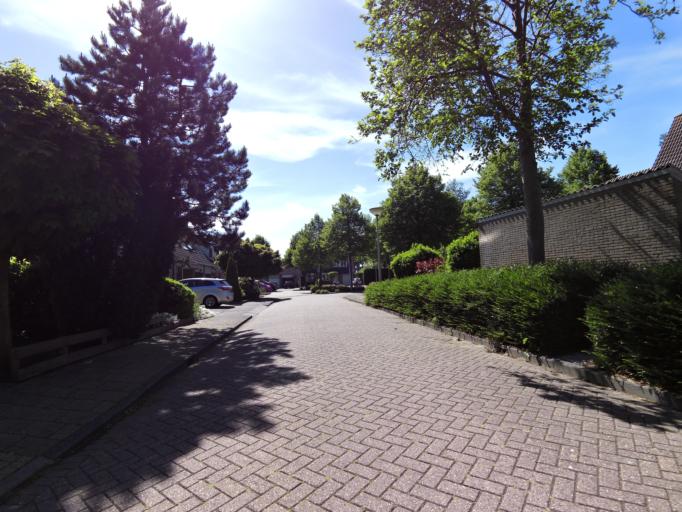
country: NL
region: South Holland
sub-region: Gemeente Hellevoetsluis
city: Nieuwenhoorn
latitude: 51.8428
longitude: 4.1493
